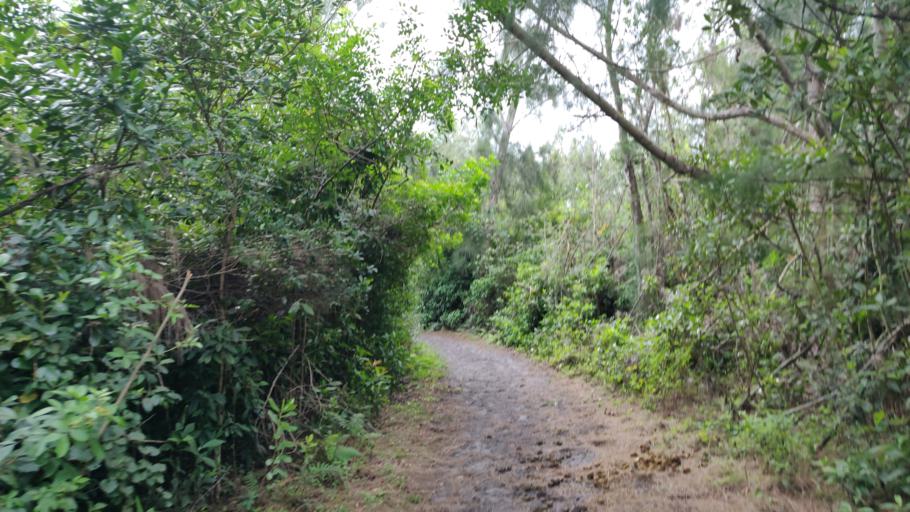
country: US
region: Florida
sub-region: Broward County
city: Cooper City
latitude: 26.0728
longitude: -80.2735
